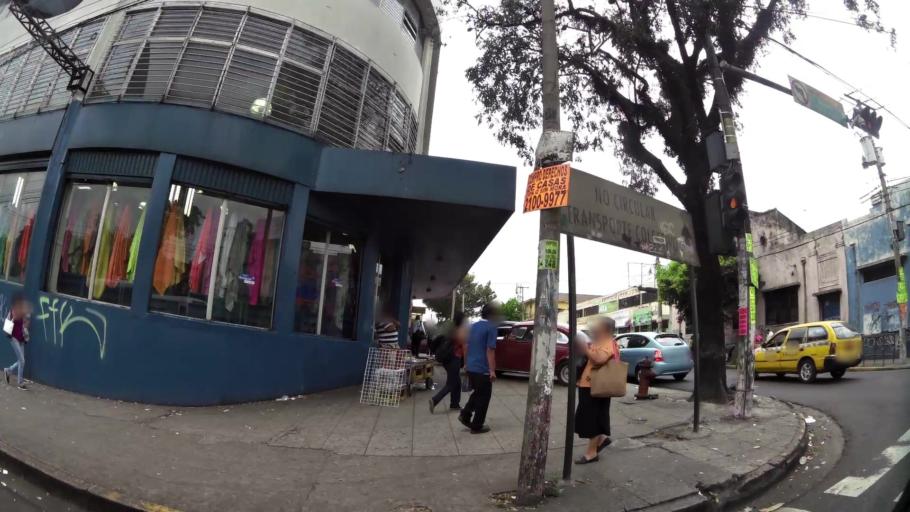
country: SV
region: San Salvador
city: San Salvador
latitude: 13.7004
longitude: -89.1966
